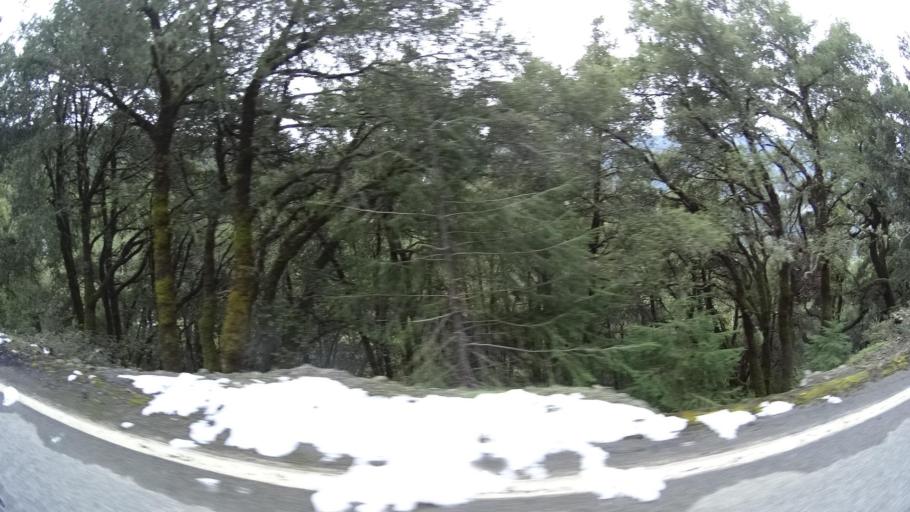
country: US
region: California
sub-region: Humboldt County
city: Willow Creek
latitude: 40.8797
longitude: -123.7610
